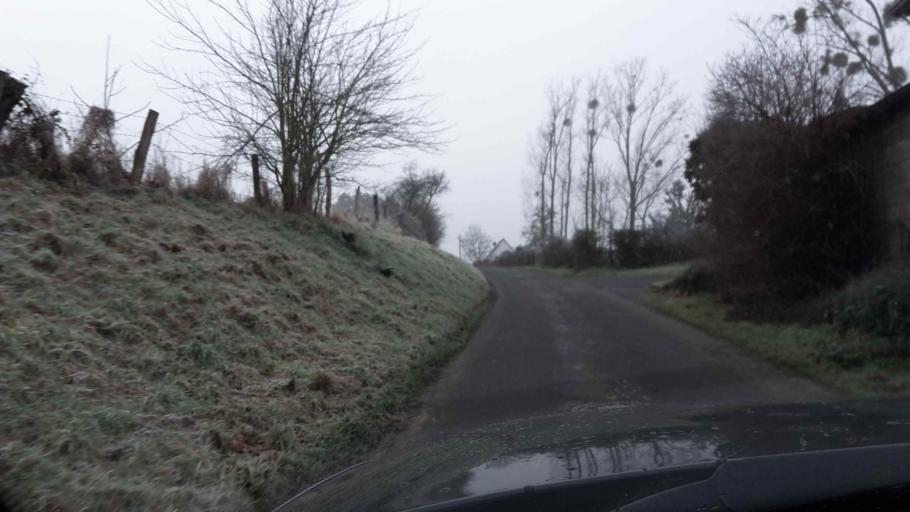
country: DE
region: North Rhine-Westphalia
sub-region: Regierungsbezirk Koln
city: Hennef
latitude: 50.7195
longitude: 7.3023
